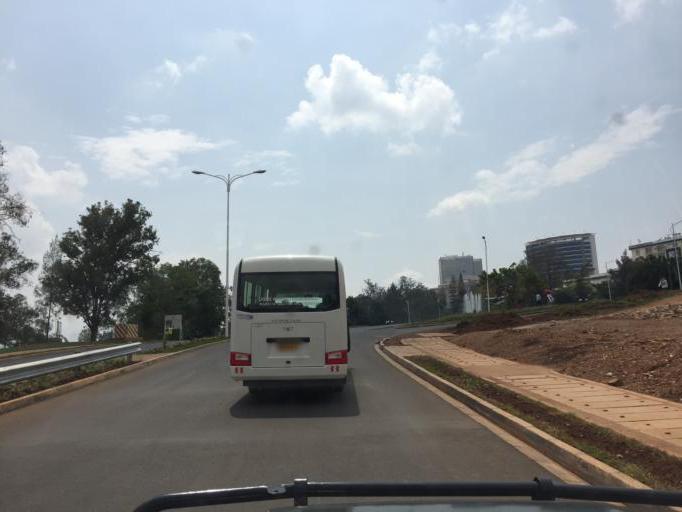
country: RW
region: Kigali
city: Kigali
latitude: -1.9429
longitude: 30.0620
